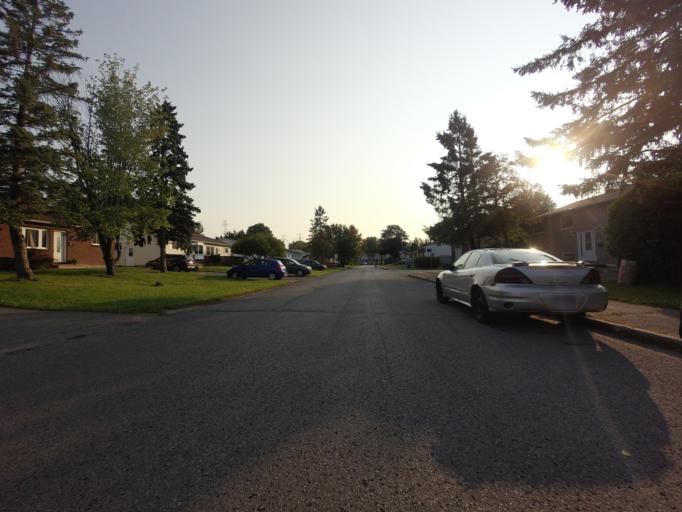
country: CA
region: Ontario
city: Bells Corners
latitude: 45.2854
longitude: -75.8791
